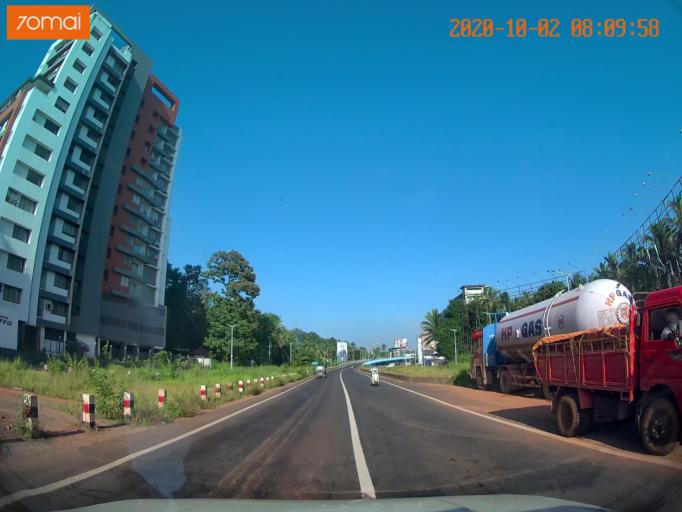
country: IN
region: Kerala
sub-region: Kozhikode
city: Kozhikode
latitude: 11.2634
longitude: 75.8155
